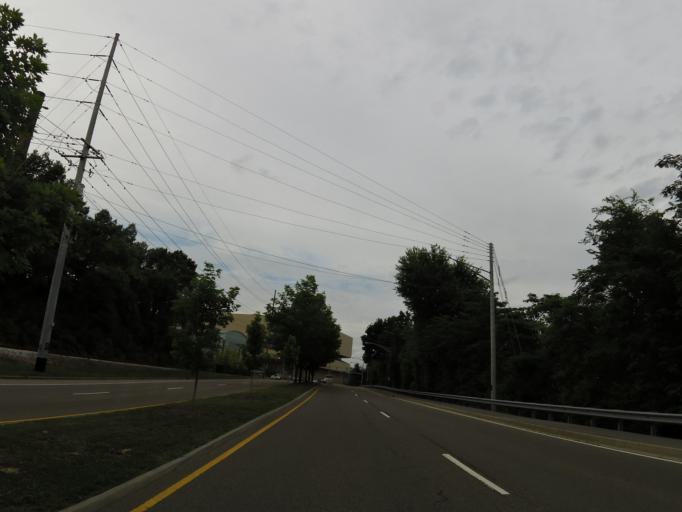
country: US
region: Tennessee
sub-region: Knox County
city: Knoxville
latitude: 35.9476
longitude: -83.9252
